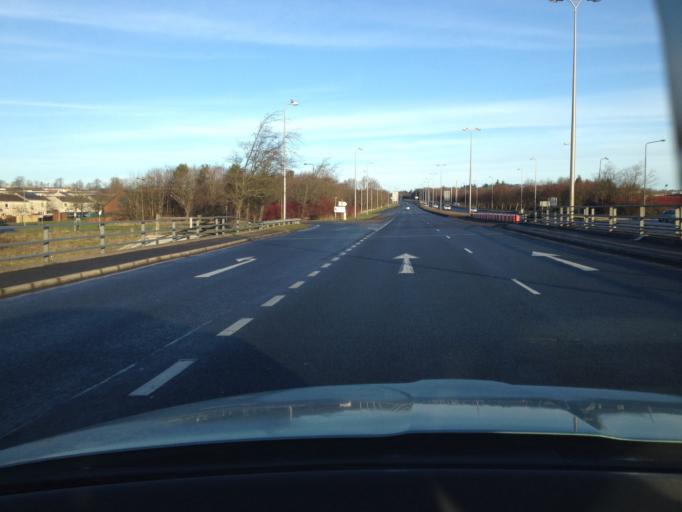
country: GB
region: Scotland
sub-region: West Lothian
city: Mid Calder
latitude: 55.8903
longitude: -3.5028
